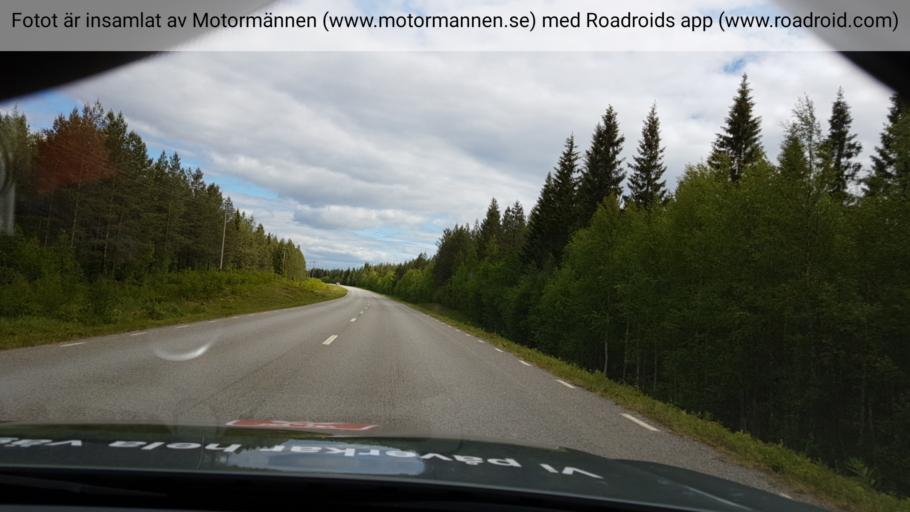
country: SE
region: Jaemtland
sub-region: Stroemsunds Kommun
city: Stroemsund
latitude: 64.2859
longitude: 15.3508
